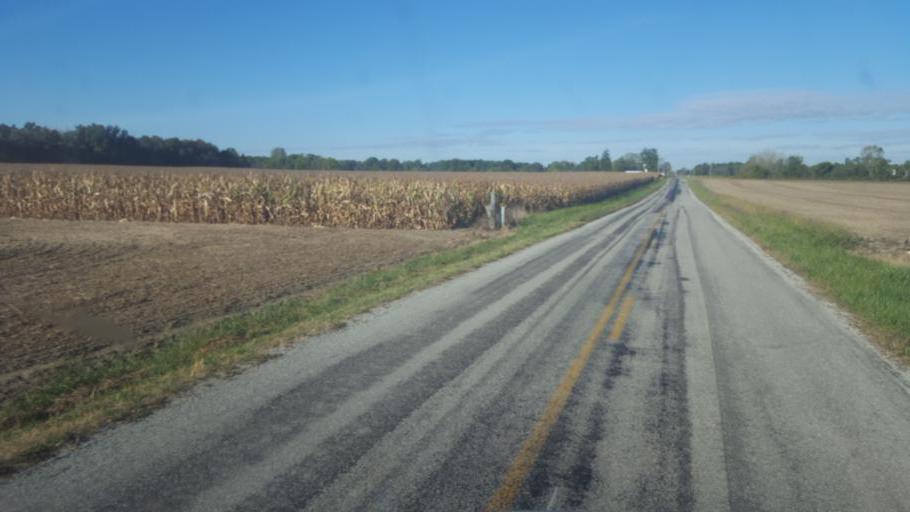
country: US
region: Ohio
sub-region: Crawford County
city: Galion
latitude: 40.6898
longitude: -82.9143
